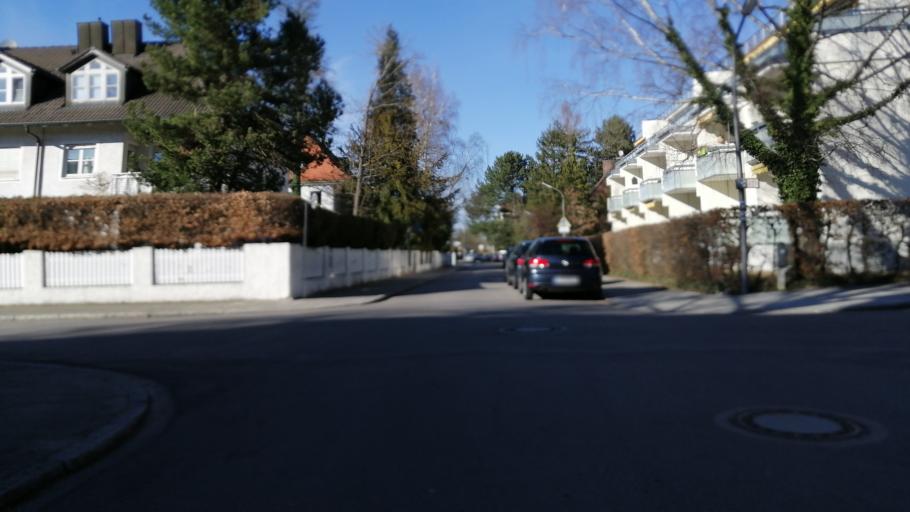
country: DE
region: Bavaria
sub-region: Upper Bavaria
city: Neuried
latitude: 48.1156
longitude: 11.5076
